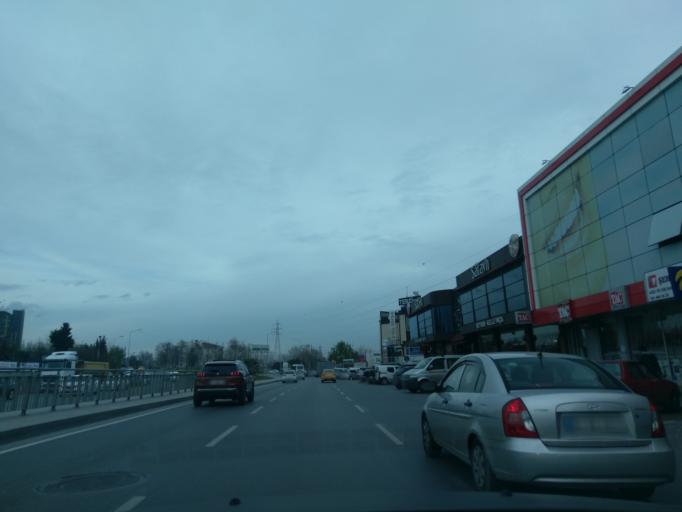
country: TR
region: Istanbul
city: Mahmutbey
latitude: 41.0554
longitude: 28.7925
